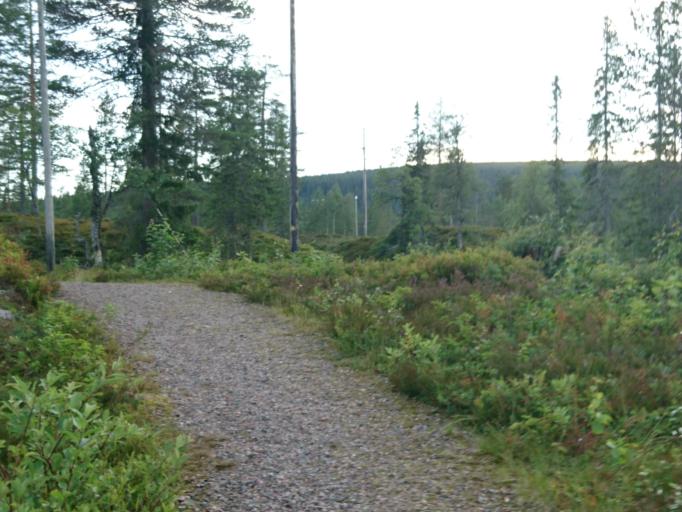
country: SE
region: Dalarna
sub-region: Malung-Saelens kommun
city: Malung
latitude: 61.1725
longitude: 13.1699
